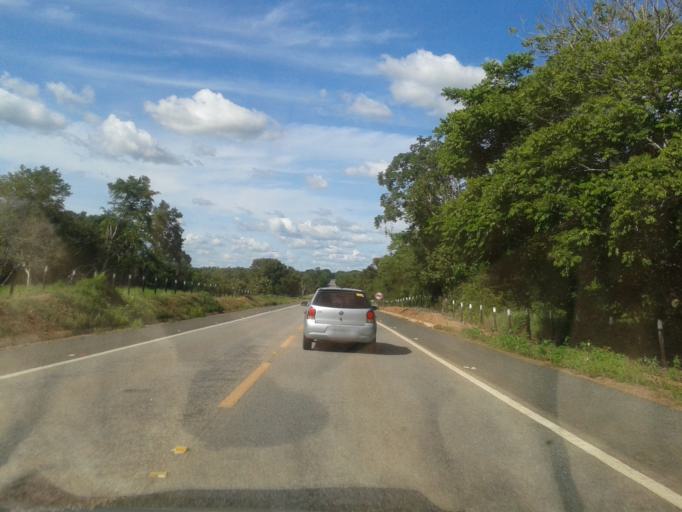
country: BR
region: Goias
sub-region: Mozarlandia
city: Mozarlandia
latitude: -15.0036
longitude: -50.5903
